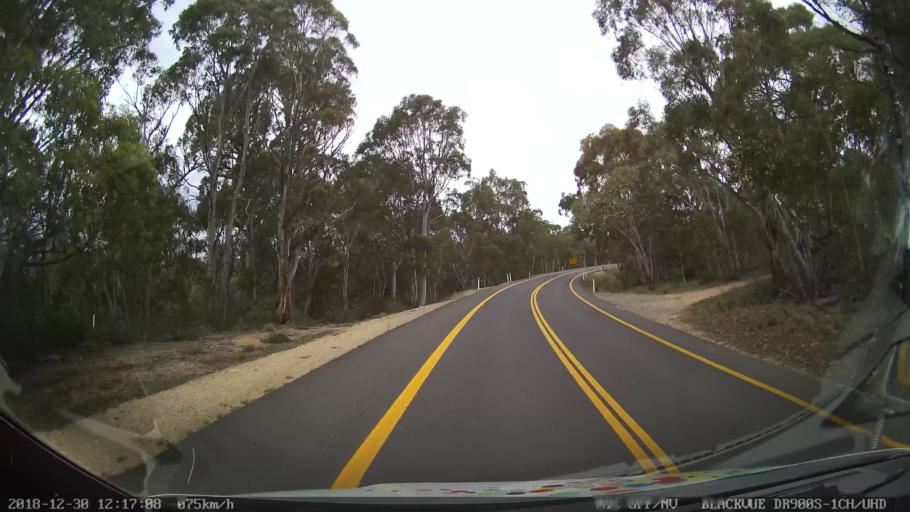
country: AU
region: New South Wales
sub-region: Snowy River
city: Jindabyne
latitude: -36.3522
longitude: 148.5636
